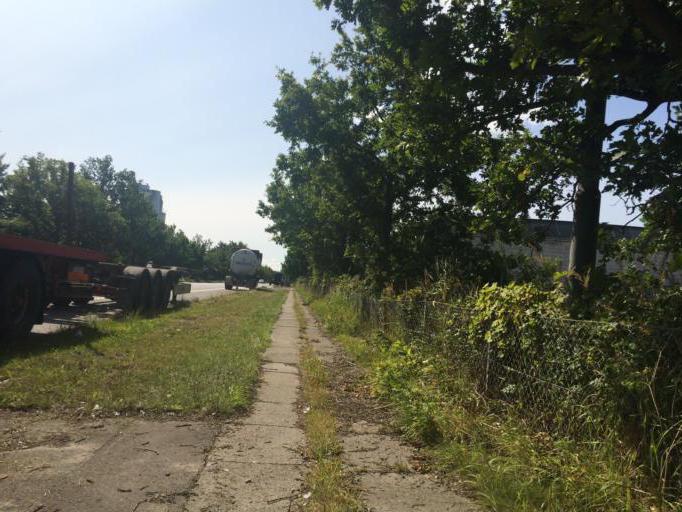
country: DK
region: Capital Region
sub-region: Hvidovre Kommune
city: Hvidovre
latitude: 55.6113
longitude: 12.4747
